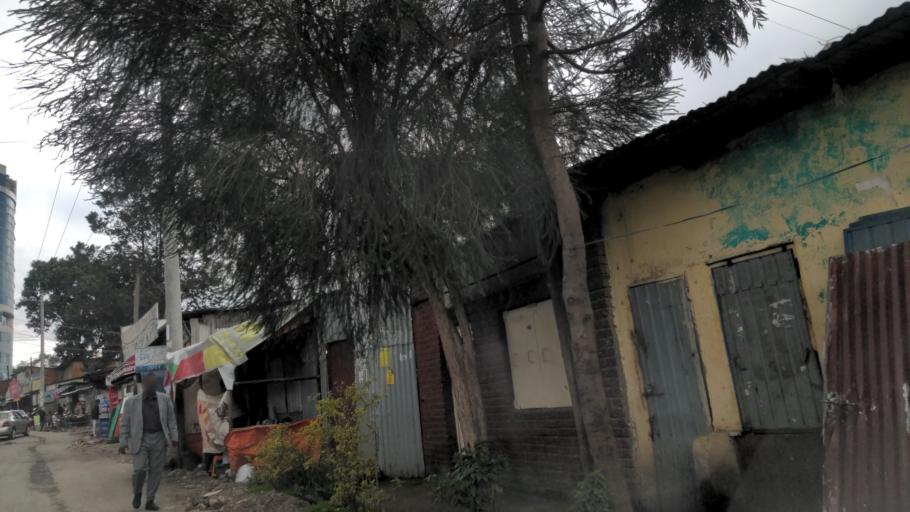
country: ET
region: Adis Abeba
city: Addis Ababa
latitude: 9.0147
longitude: 38.7883
